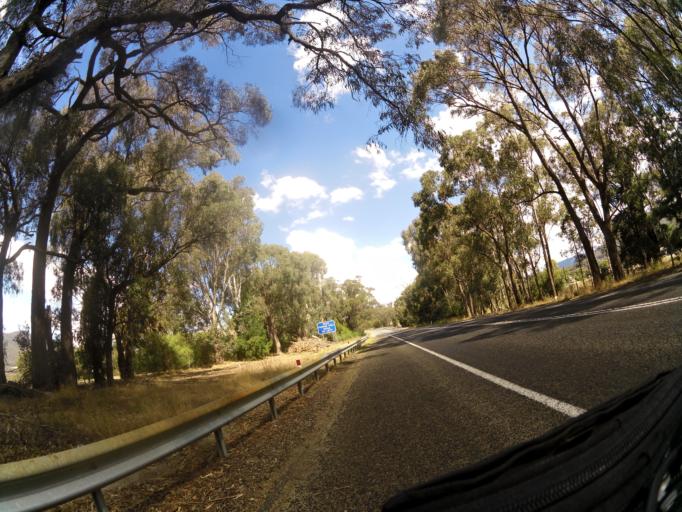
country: AU
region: Victoria
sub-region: Mansfield
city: Mansfield
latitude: -36.8353
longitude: 146.0077
